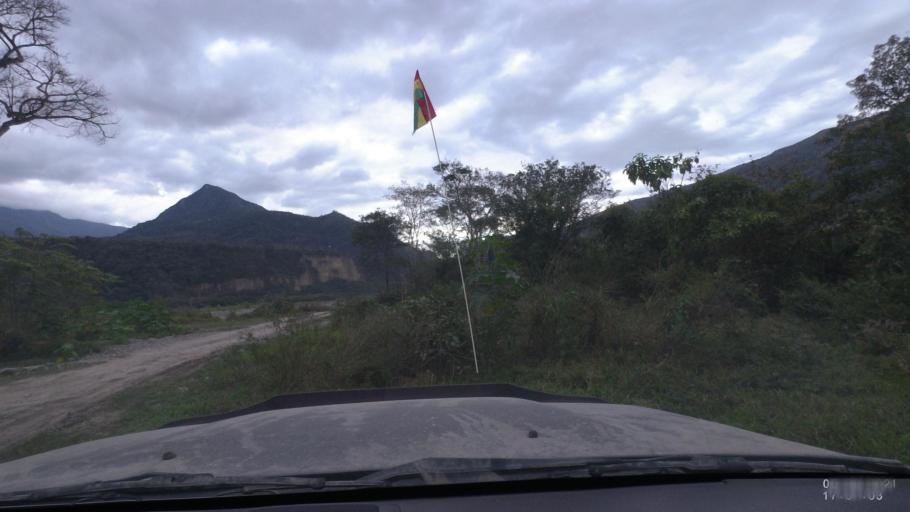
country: BO
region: La Paz
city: Quime
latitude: -16.4764
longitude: -66.7888
